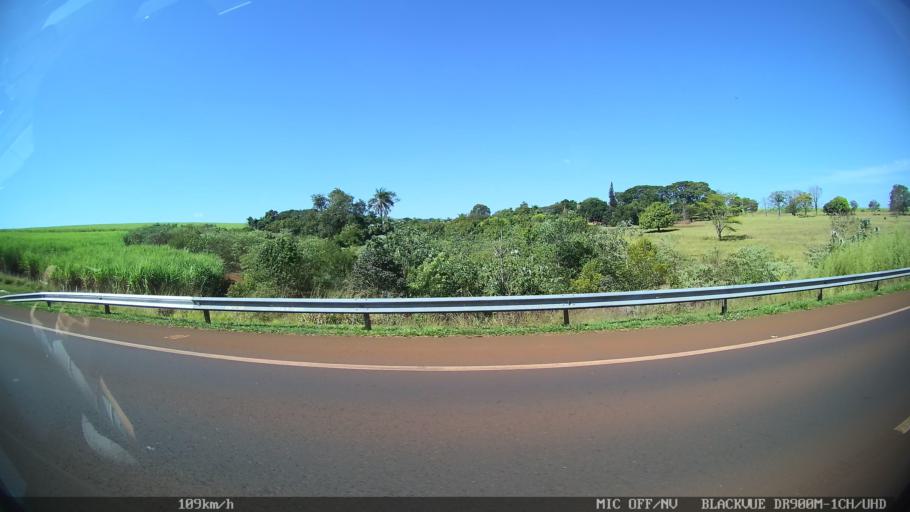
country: BR
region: Sao Paulo
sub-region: Franca
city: Franca
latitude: -20.6557
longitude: -47.4906
